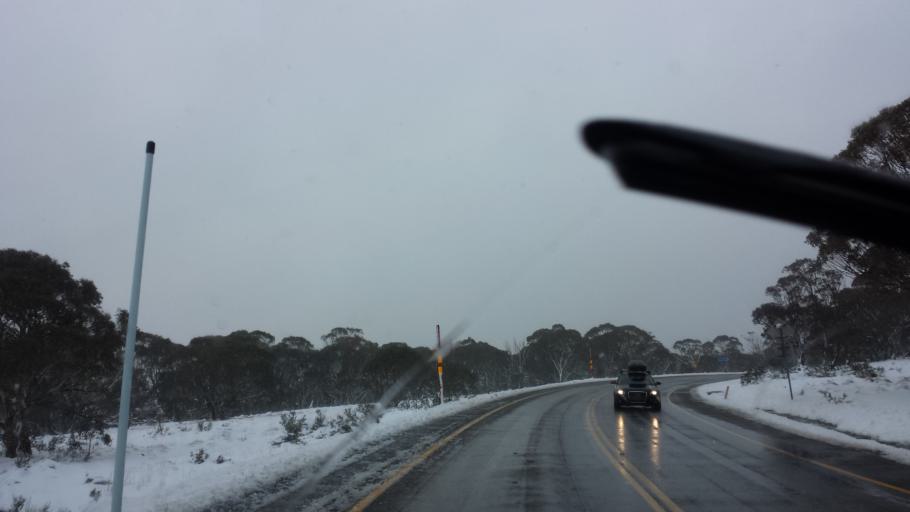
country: AU
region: Victoria
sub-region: Alpine
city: Mount Beauty
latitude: -37.0205
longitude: 147.2425
